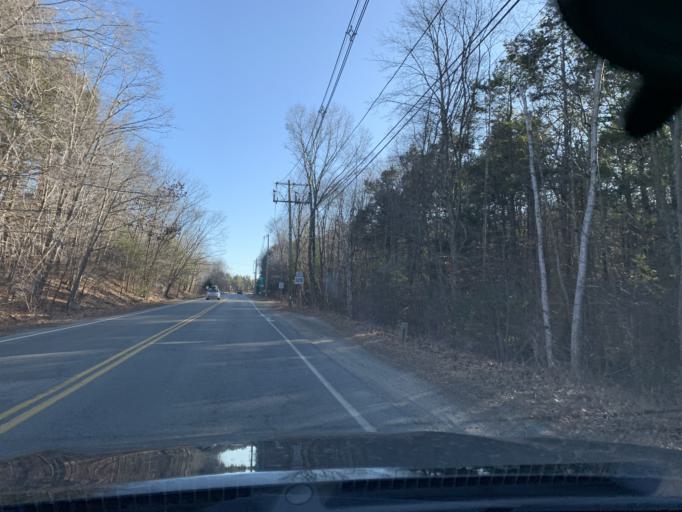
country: US
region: Massachusetts
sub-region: Essex County
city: Essex
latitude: 42.5947
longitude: -70.7670
